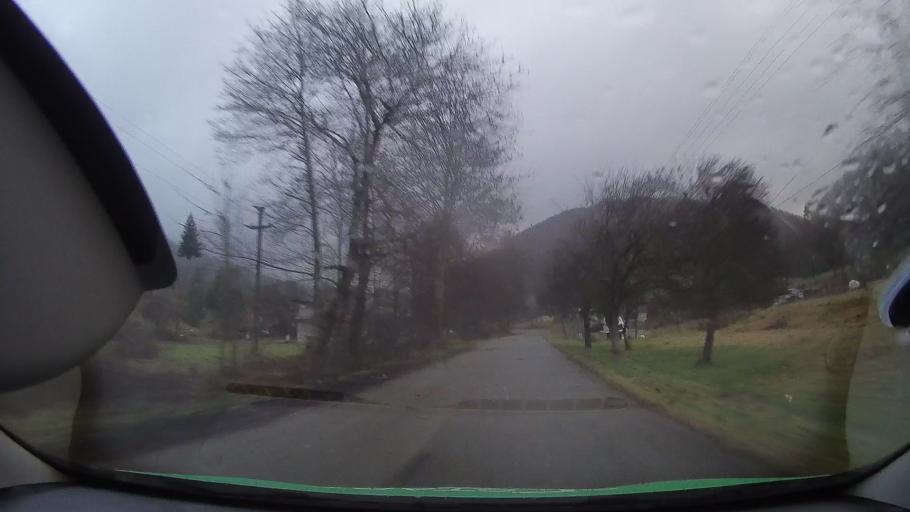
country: RO
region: Hunedoara
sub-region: Comuna Ribita
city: Ribita
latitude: 46.2565
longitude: 22.7464
